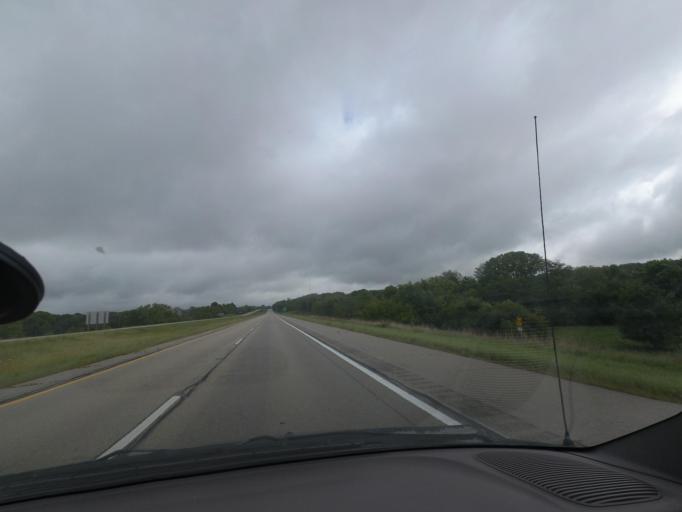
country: US
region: Illinois
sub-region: Piatt County
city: Monticello
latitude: 40.0432
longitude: -88.5842
